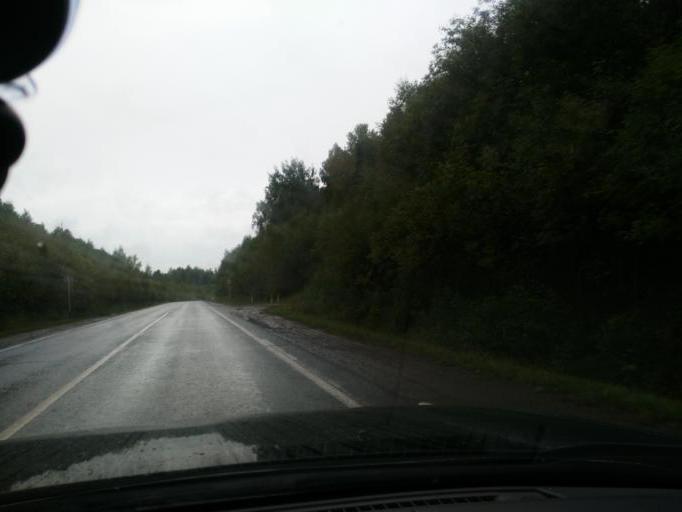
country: RU
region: Perm
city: Yugo-Kamskiy
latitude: 57.7450
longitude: 55.7125
